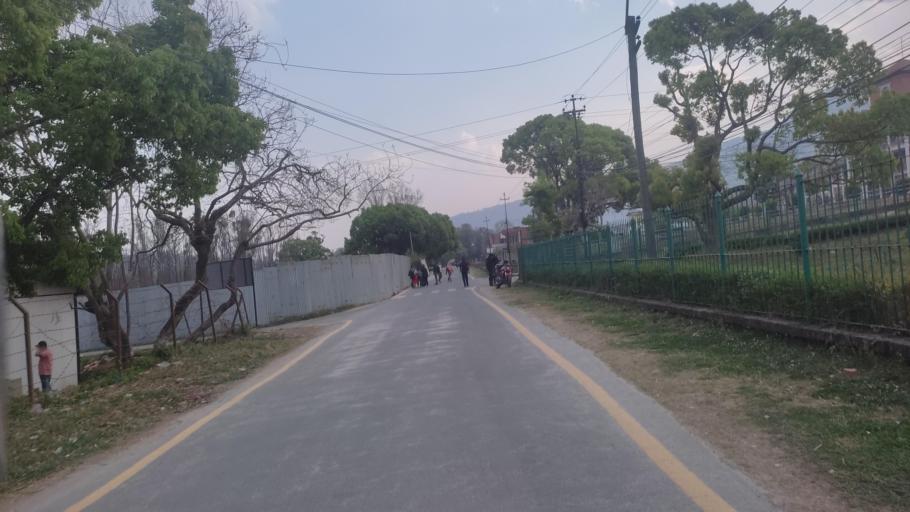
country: NP
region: Central Region
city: Kirtipur
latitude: 27.6817
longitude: 85.2844
